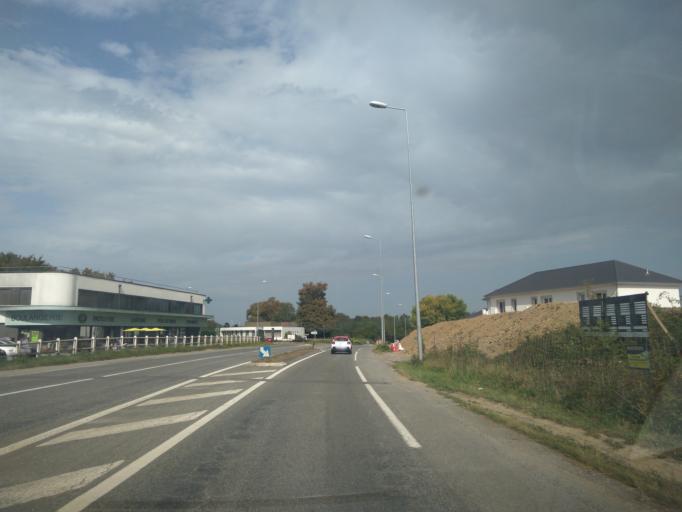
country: FR
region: Aquitaine
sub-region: Departement des Pyrenees-Atlantiques
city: Artiguelouve
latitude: 43.3173
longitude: -0.4619
